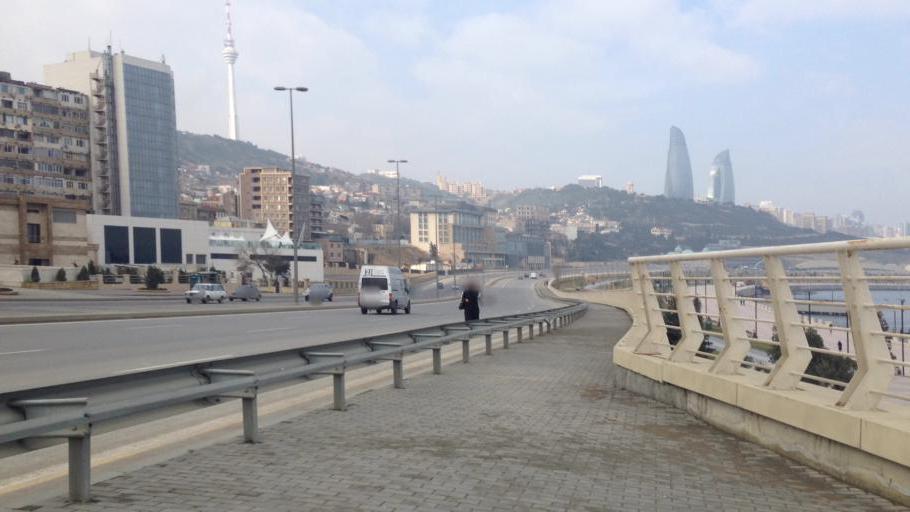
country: AZ
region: Baki
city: Badamdar
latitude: 40.3457
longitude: 49.8410
